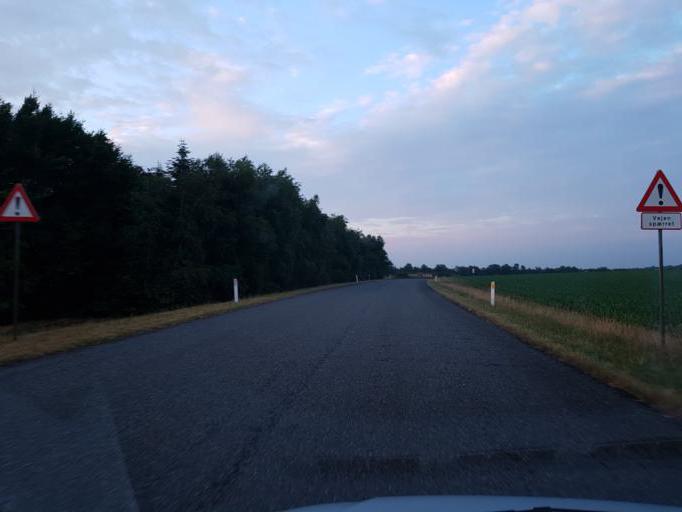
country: DK
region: South Denmark
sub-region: Esbjerg Kommune
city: Tjaereborg
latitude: 55.5203
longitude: 8.5723
